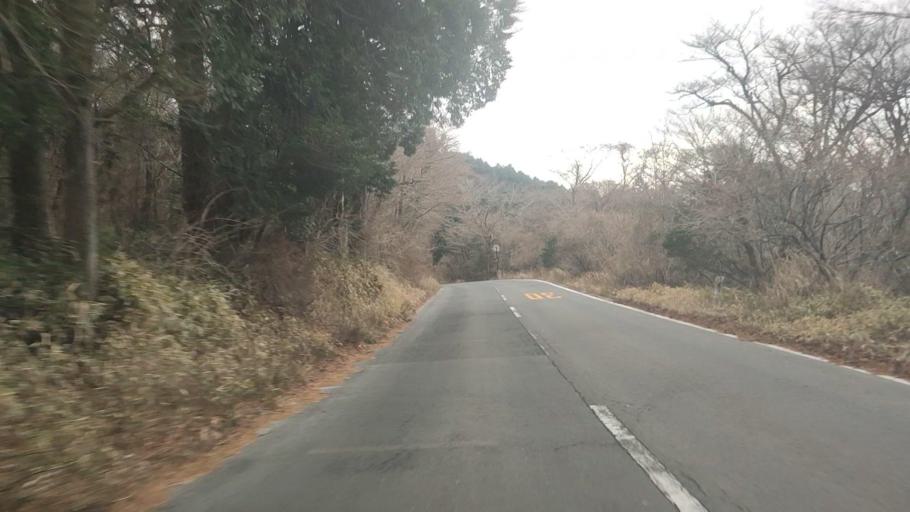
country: JP
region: Nagasaki
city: Shimabara
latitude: 32.7546
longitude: 130.2769
